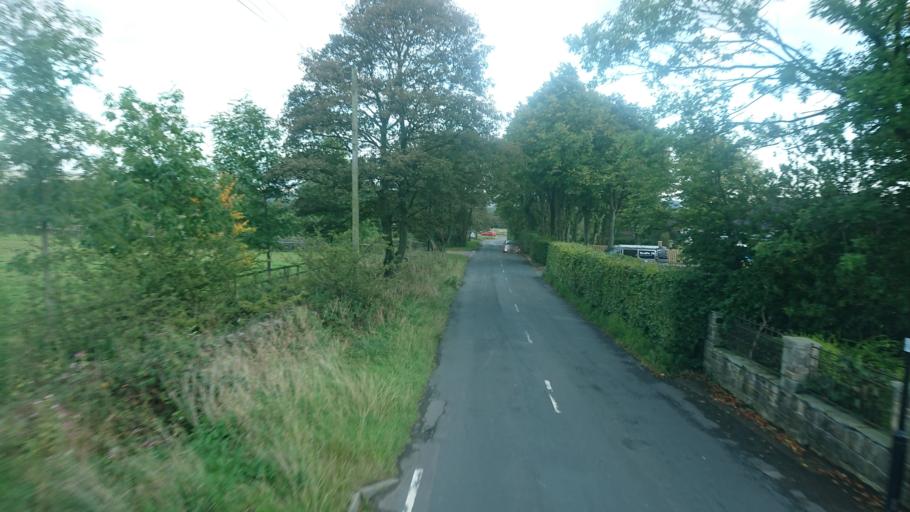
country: GB
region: England
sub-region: Derbyshire
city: Dronfield
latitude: 53.3365
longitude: -1.5472
